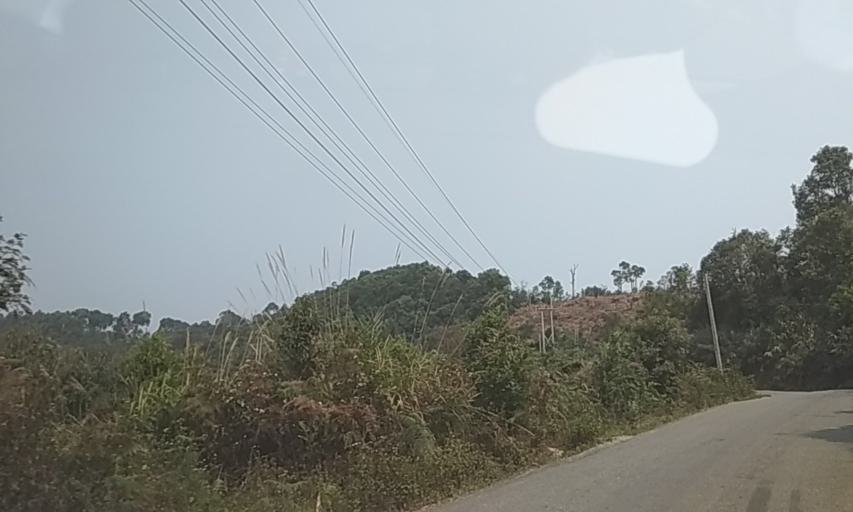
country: TH
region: Nan
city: Chaloem Phra Kiat
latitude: 20.0218
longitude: 101.1014
